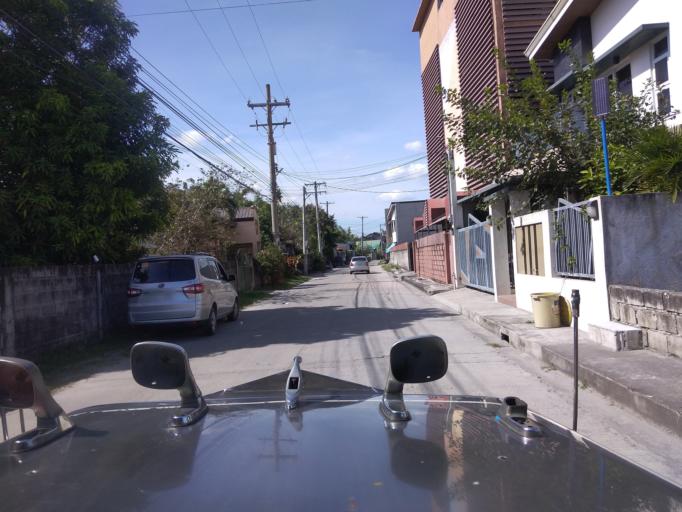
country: PH
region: Central Luzon
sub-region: Province of Pampanga
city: San Juan
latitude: 15.0251
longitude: 120.6707
